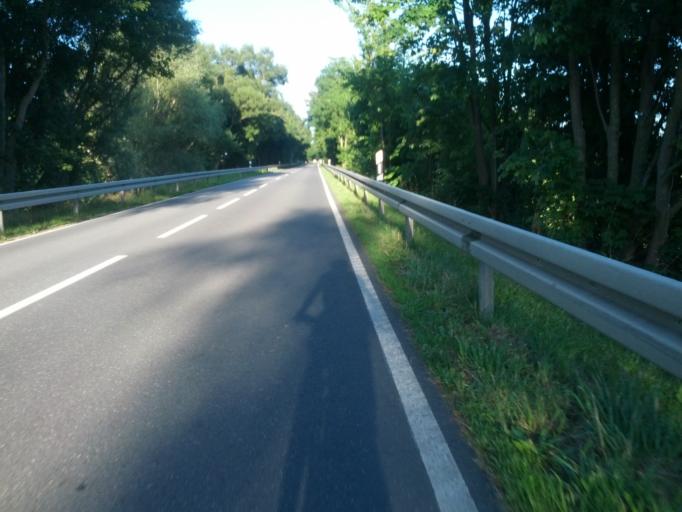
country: DE
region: Mecklenburg-Vorpommern
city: Bastorf
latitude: 54.1080
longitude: 11.6623
